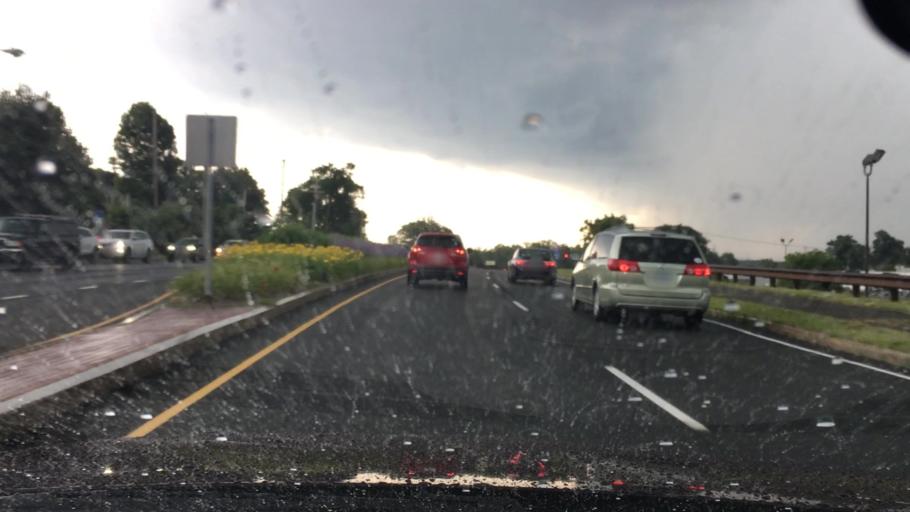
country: US
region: Connecticut
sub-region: Hartford County
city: Manchester
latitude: 41.7983
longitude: -72.5509
